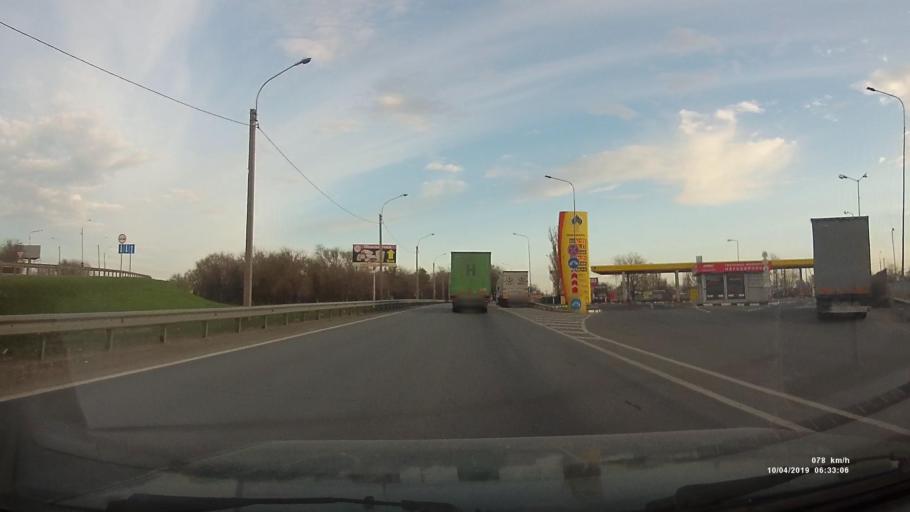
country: RU
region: Rostov
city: Aksay
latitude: 47.2825
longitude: 39.8503
